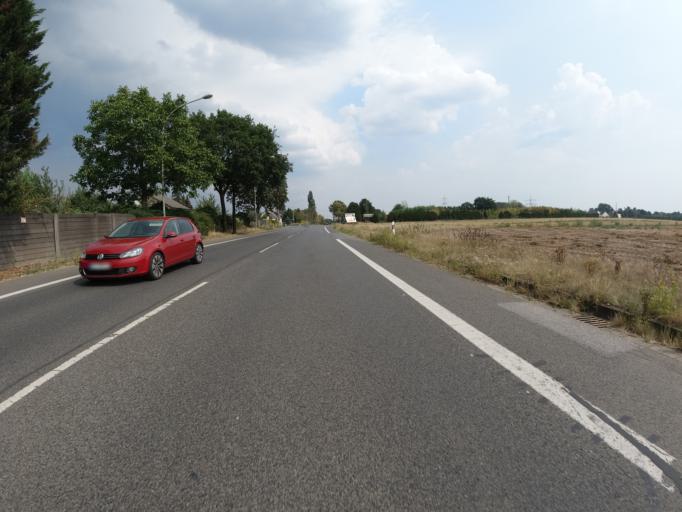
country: DE
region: North Rhine-Westphalia
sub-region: Regierungsbezirk Dusseldorf
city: Moers
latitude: 51.3943
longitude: 6.6344
